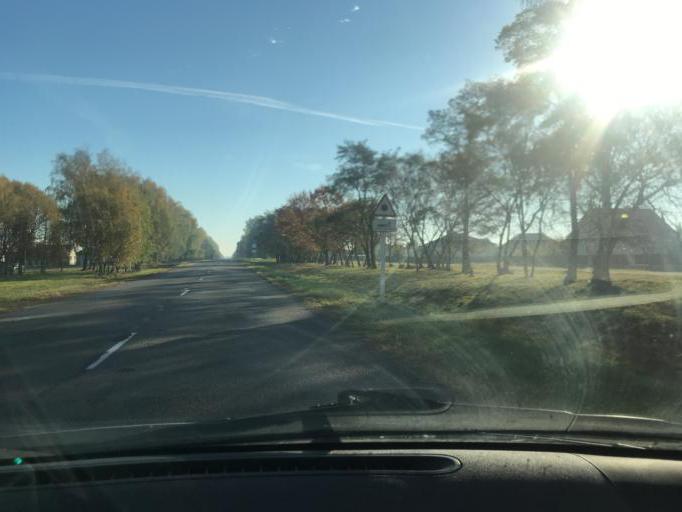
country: BY
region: Brest
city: Ivanava
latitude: 52.1446
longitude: 25.4906
